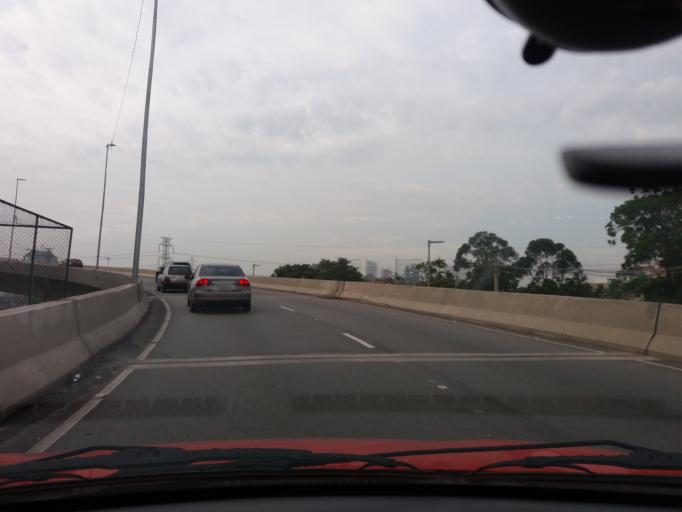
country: BR
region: Sao Paulo
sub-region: Taboao Da Serra
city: Taboao da Serra
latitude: -23.6402
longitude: -46.7276
